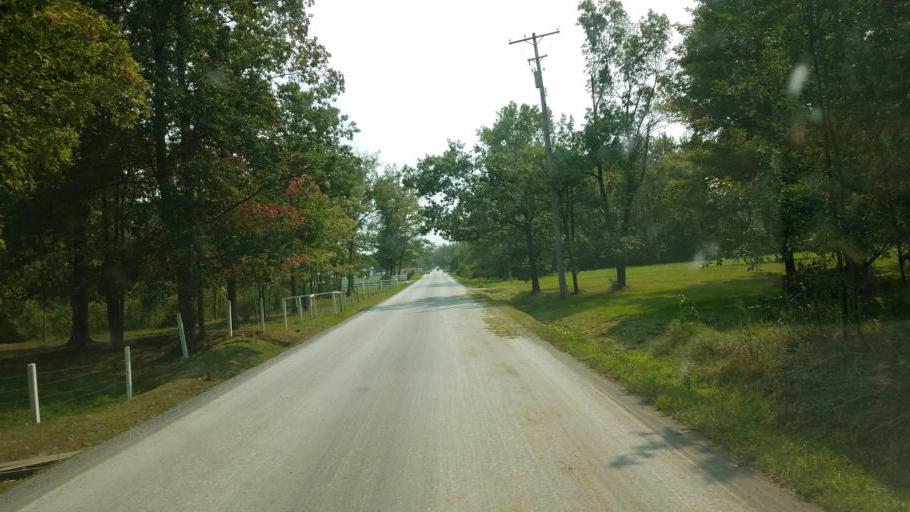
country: US
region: Ohio
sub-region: Geauga County
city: Middlefield
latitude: 41.5137
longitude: -81.0030
